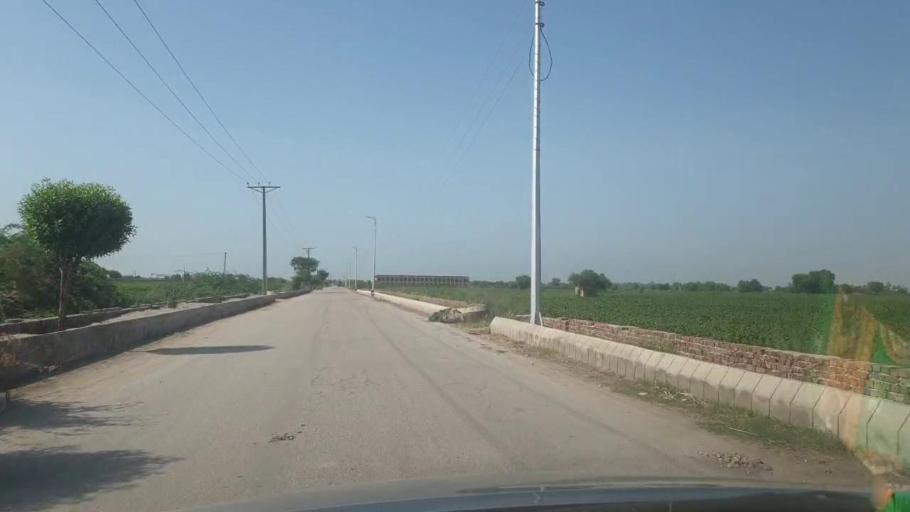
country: PK
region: Sindh
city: Rohri
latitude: 27.5200
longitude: 69.0362
